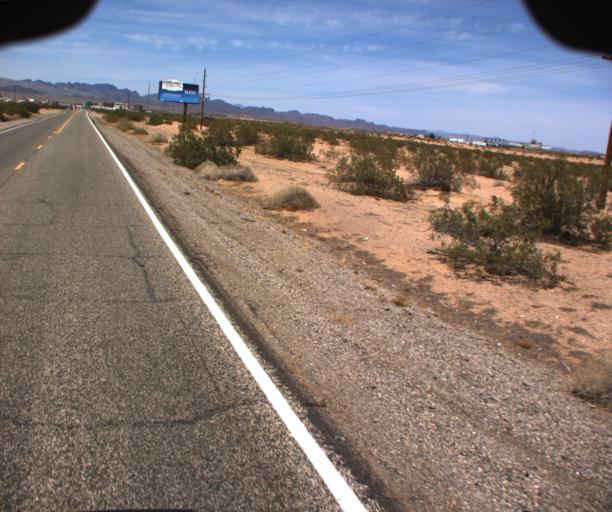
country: US
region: Arizona
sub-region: La Paz County
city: Parker
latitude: 34.1240
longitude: -114.2792
